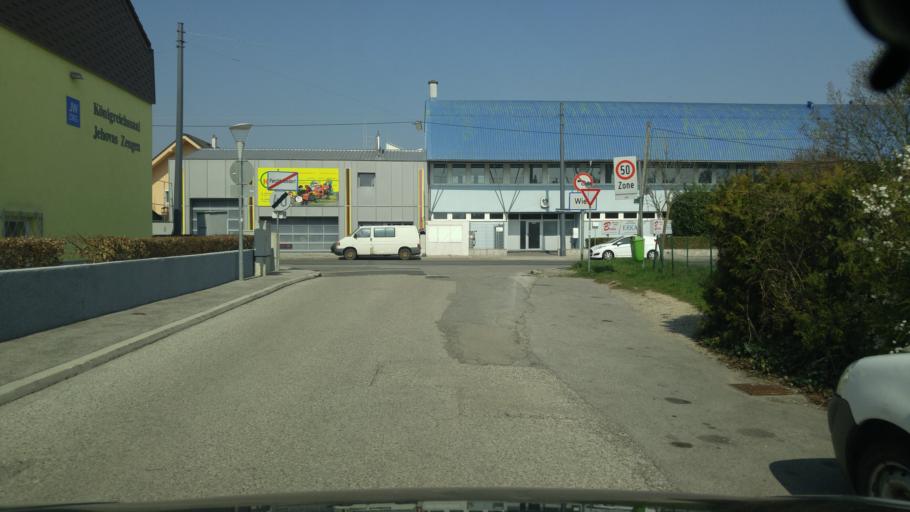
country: AT
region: Lower Austria
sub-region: Politischer Bezirk Modling
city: Brunn am Gebirge
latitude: 48.1301
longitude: 16.2909
